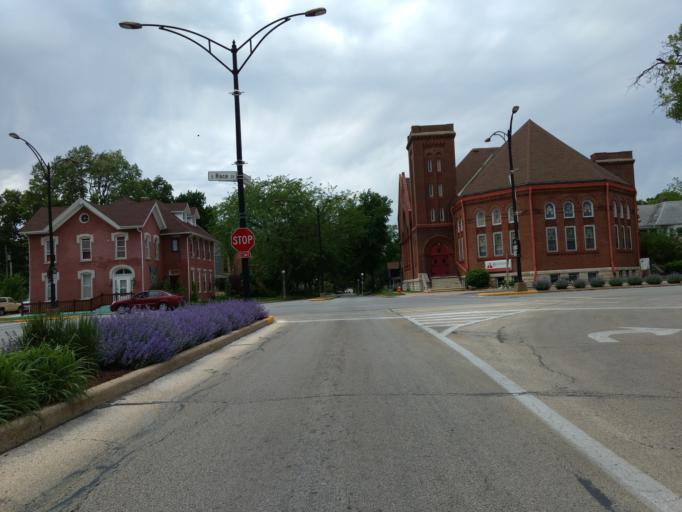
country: US
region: Illinois
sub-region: Champaign County
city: Urbana
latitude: 40.1092
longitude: -88.2085
